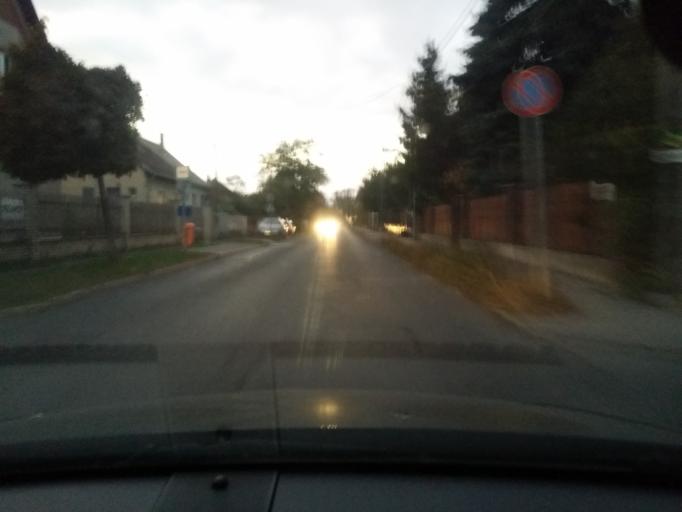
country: HU
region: Budapest
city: Budapest XVI. keruelet
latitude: 47.5243
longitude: 19.1501
